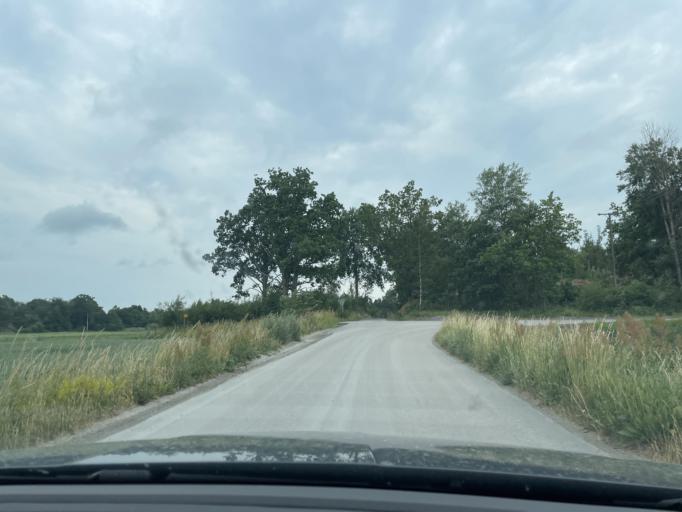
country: SE
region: Blekinge
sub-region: Karlshamns Kommun
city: Morrum
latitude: 56.1653
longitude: 14.7392
